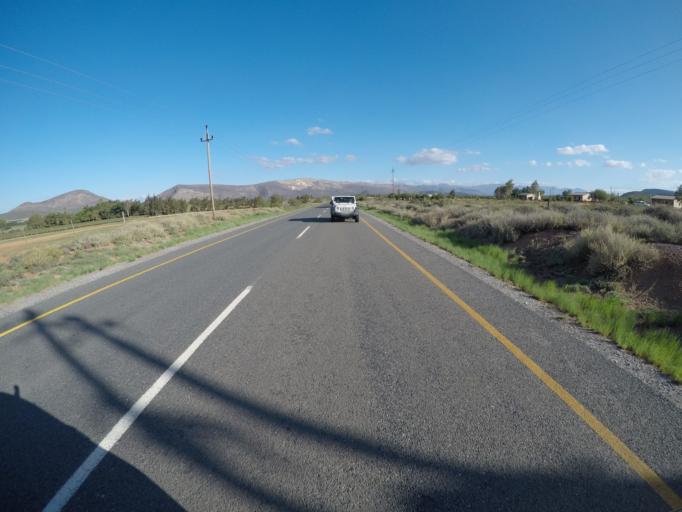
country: ZA
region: Western Cape
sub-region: Cape Winelands District Municipality
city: Ashton
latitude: -33.8002
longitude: 19.7814
